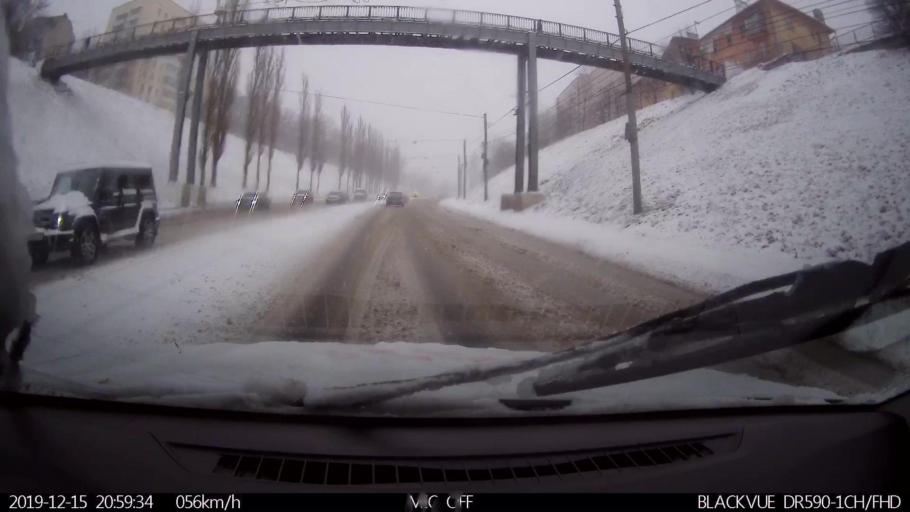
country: RU
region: Nizjnij Novgorod
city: Nizhniy Novgorod
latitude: 56.3203
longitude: 43.9800
